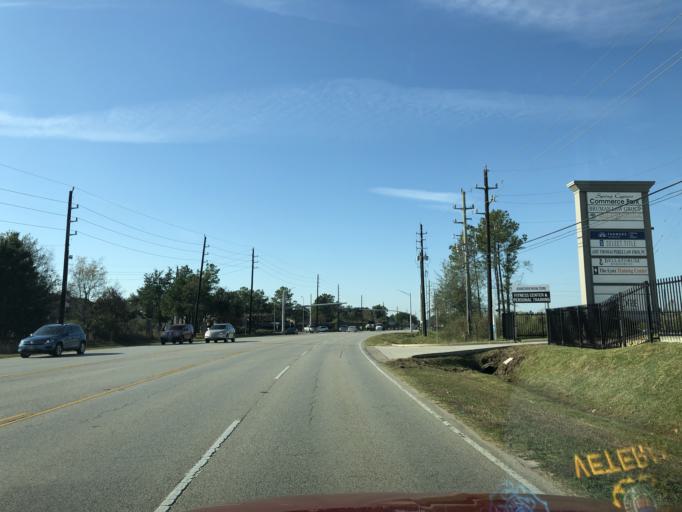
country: US
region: Texas
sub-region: Harris County
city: Tomball
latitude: 30.0393
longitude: -95.5473
